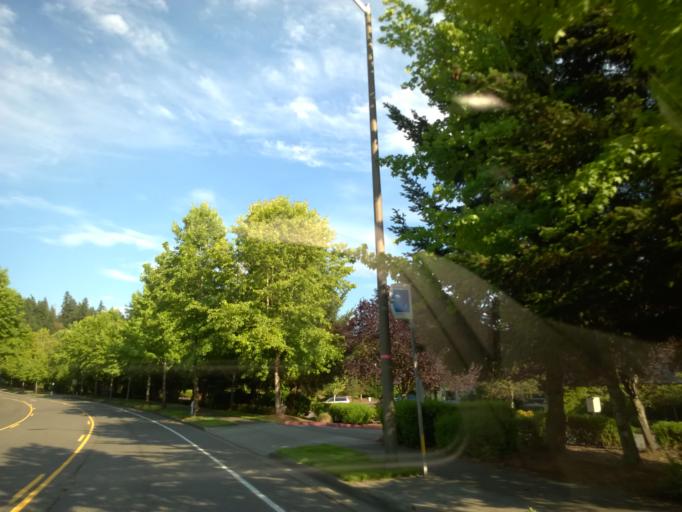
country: US
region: Washington
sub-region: King County
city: Bothell
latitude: 47.7781
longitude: -122.1827
